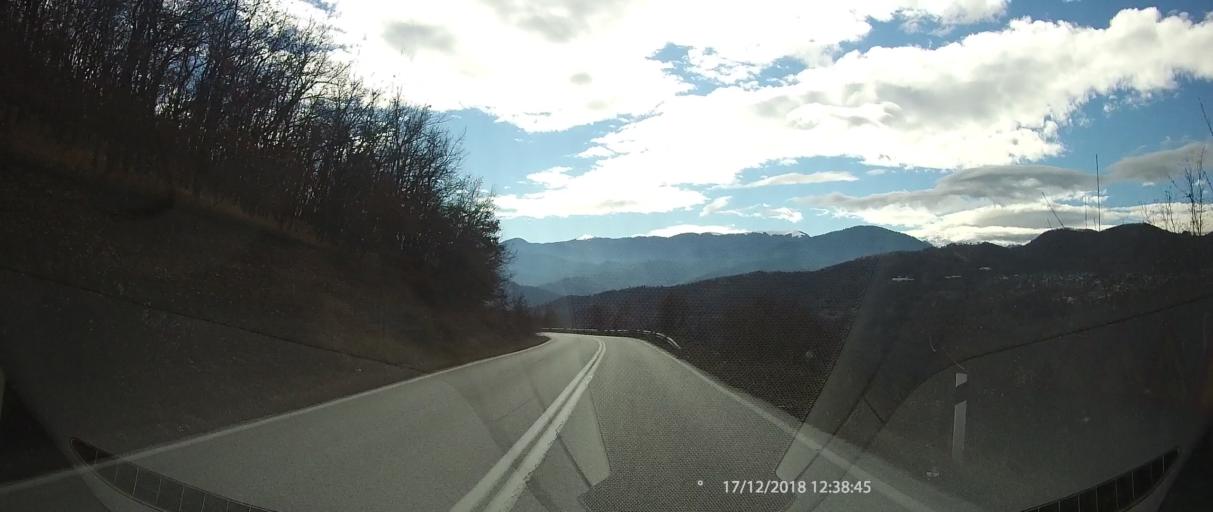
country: GR
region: Epirus
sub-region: Nomos Ioanninon
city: Metsovo
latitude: 39.8057
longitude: 21.3490
